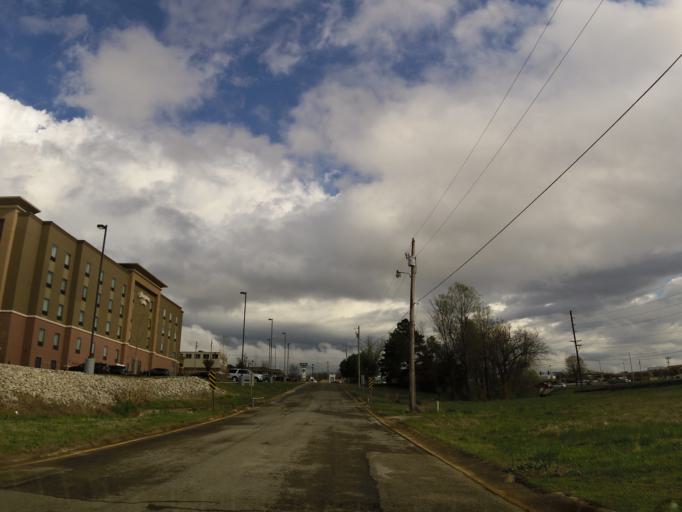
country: US
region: Missouri
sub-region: Butler County
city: Poplar Bluff
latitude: 36.7825
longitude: -90.4288
